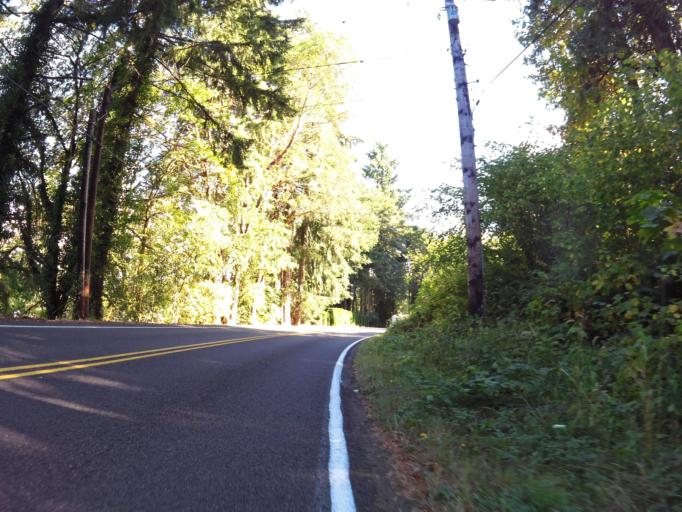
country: US
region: Washington
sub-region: Thurston County
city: Olympia
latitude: 47.0623
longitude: -123.0142
